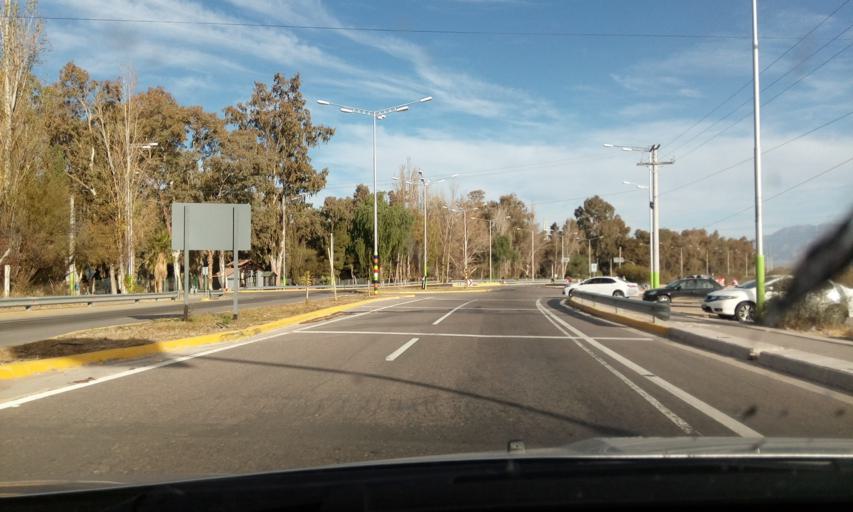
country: AR
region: San Juan
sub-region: Departamento de Rivadavia
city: Rivadavia
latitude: -31.5050
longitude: -68.6451
